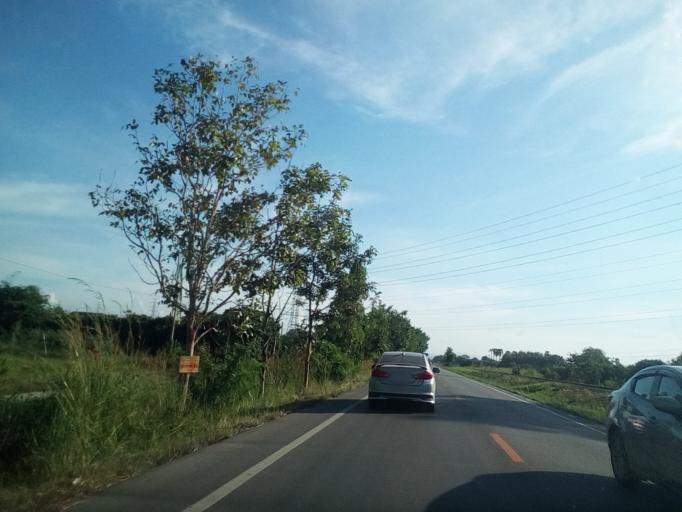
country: TH
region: Chiang Mai
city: Saraphi
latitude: 18.6605
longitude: 99.0446
